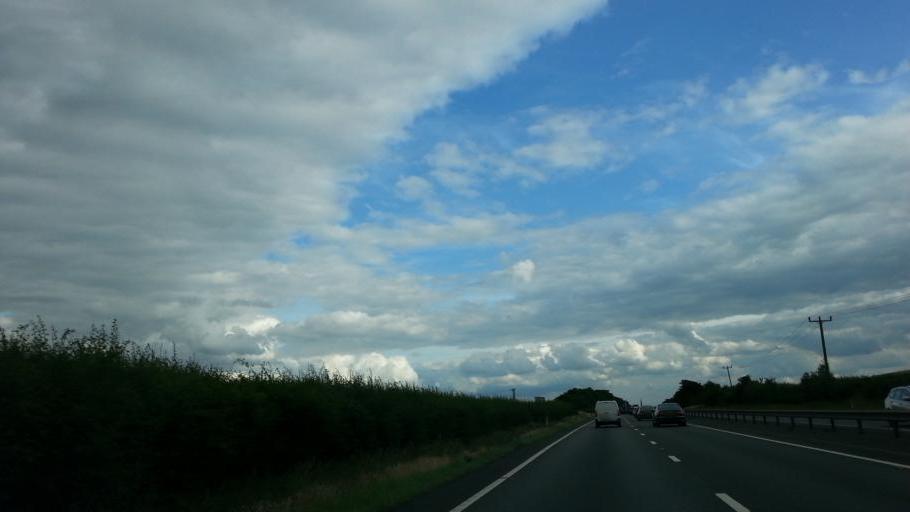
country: GB
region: England
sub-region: Nottinghamshire
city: South Collingham
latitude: 53.1811
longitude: -0.8208
